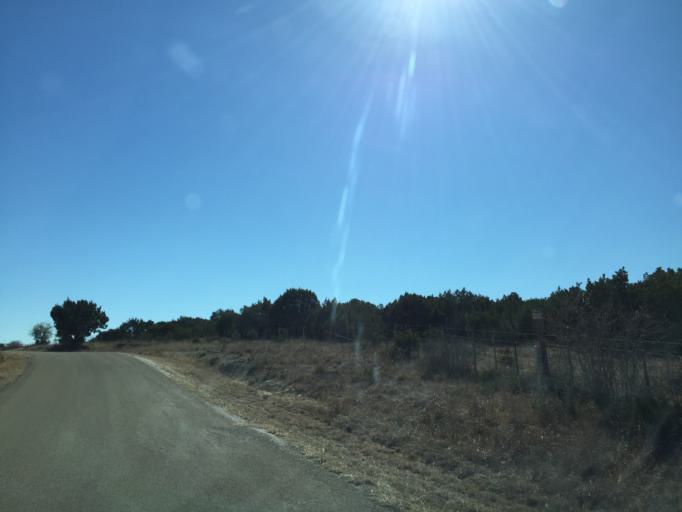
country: US
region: Texas
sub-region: Burnet County
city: Bertram
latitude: 30.8937
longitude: -98.1213
